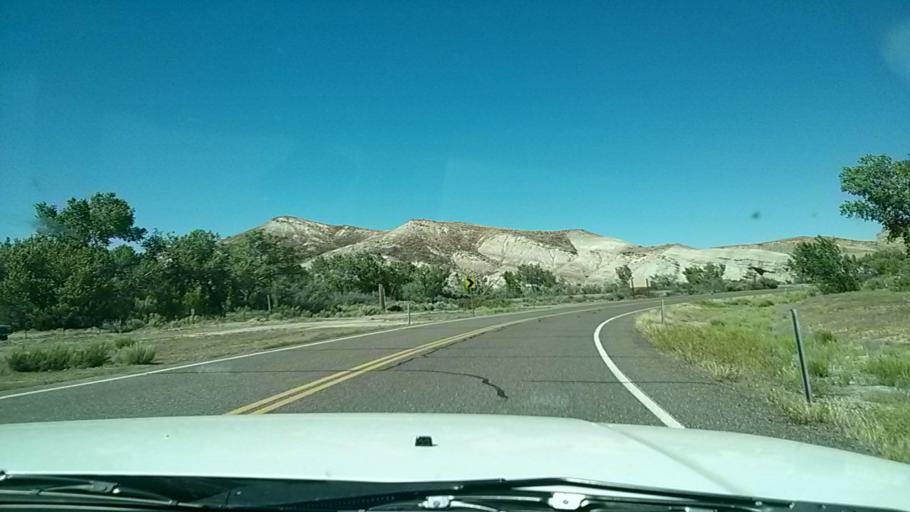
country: US
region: Utah
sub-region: Wayne County
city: Loa
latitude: 38.2913
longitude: -111.0475
